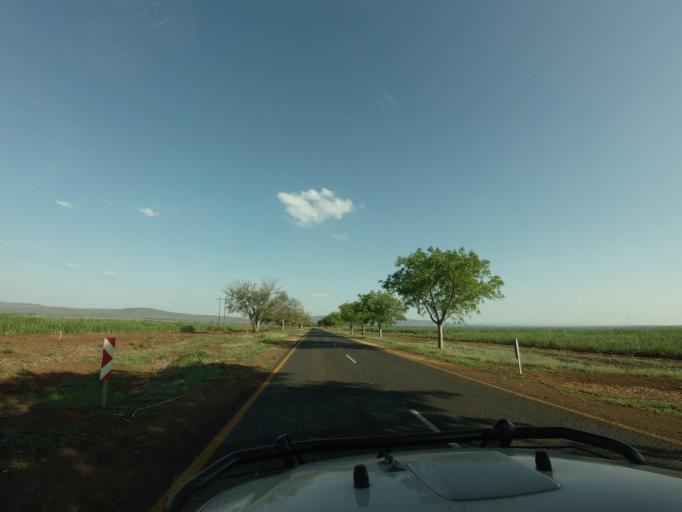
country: ZA
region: Mpumalanga
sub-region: Ehlanzeni District
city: Komatipoort
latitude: -25.4032
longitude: 31.9247
